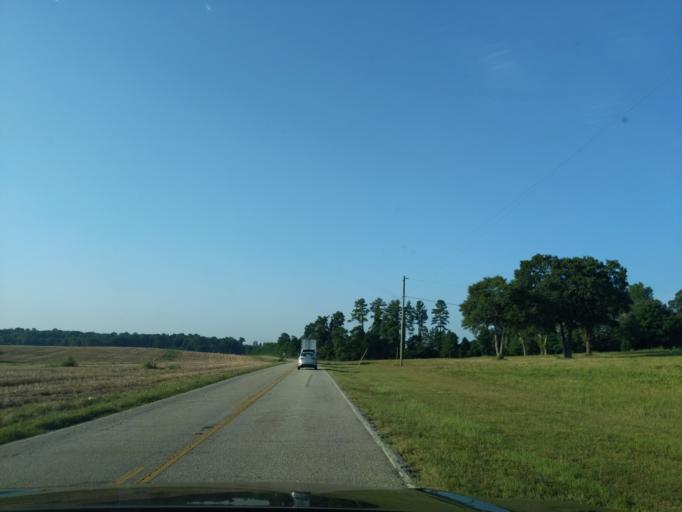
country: US
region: South Carolina
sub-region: Spartanburg County
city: Roebuck
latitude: 34.8179
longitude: -81.9863
